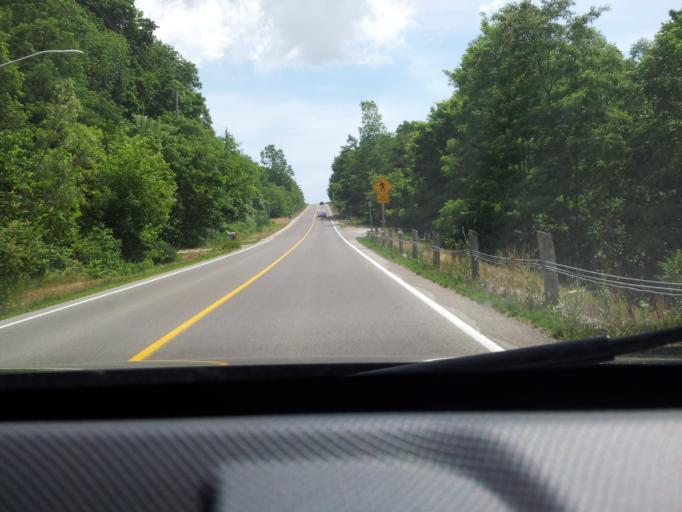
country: CA
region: Ontario
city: Norfolk County
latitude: 42.8236
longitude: -80.2875
